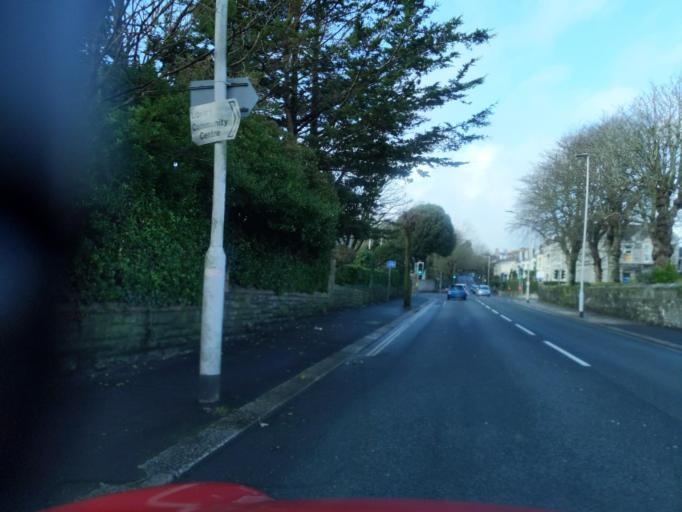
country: GB
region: England
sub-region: Plymouth
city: Plymouth
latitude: 50.3722
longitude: -4.1275
